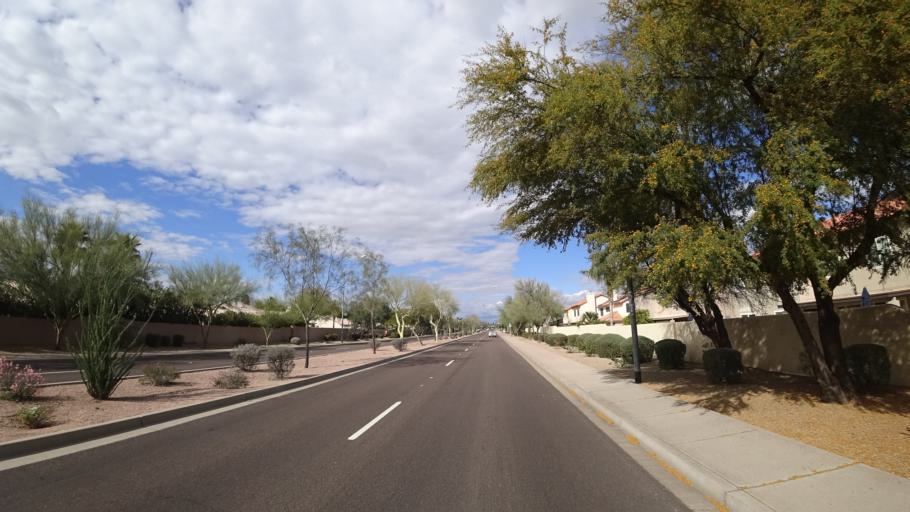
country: US
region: Arizona
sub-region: Maricopa County
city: Paradise Valley
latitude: 33.6088
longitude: -111.8783
